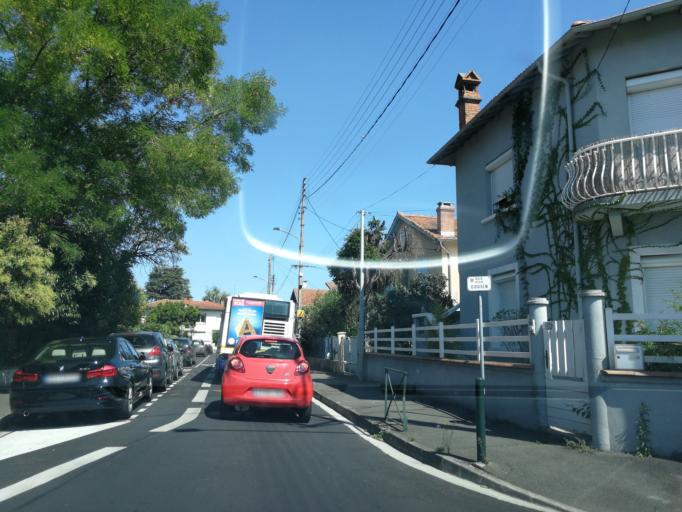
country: FR
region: Midi-Pyrenees
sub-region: Departement de la Haute-Garonne
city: L'Union
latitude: 43.6300
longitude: 1.4726
